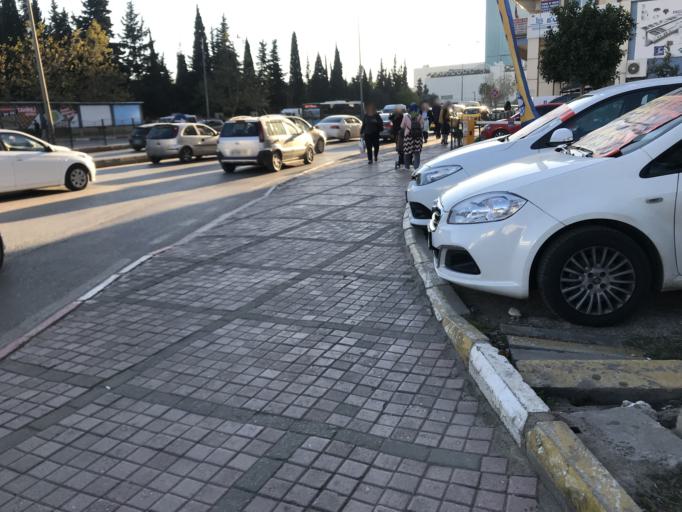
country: TR
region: Antalya
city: Antalya
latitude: 36.8955
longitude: 30.7070
